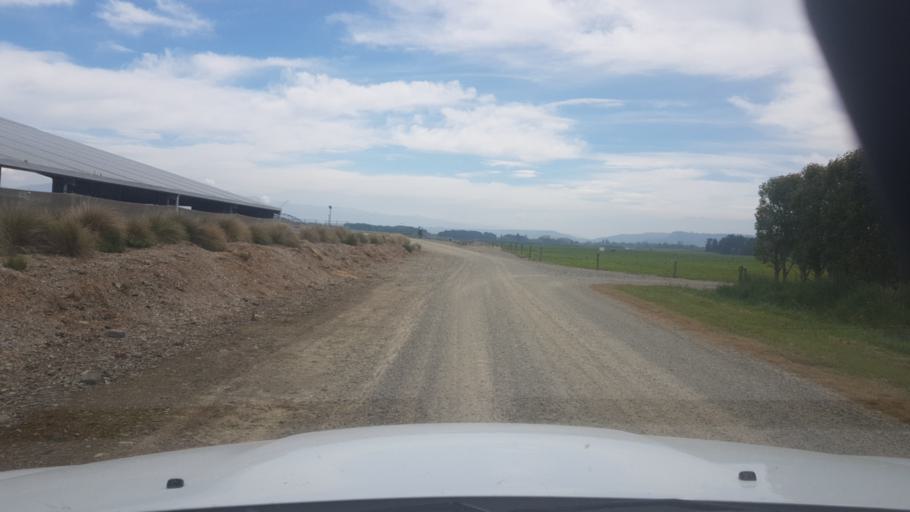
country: NZ
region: Canterbury
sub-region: Timaru District
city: Timaru
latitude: -44.4732
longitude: 171.1704
